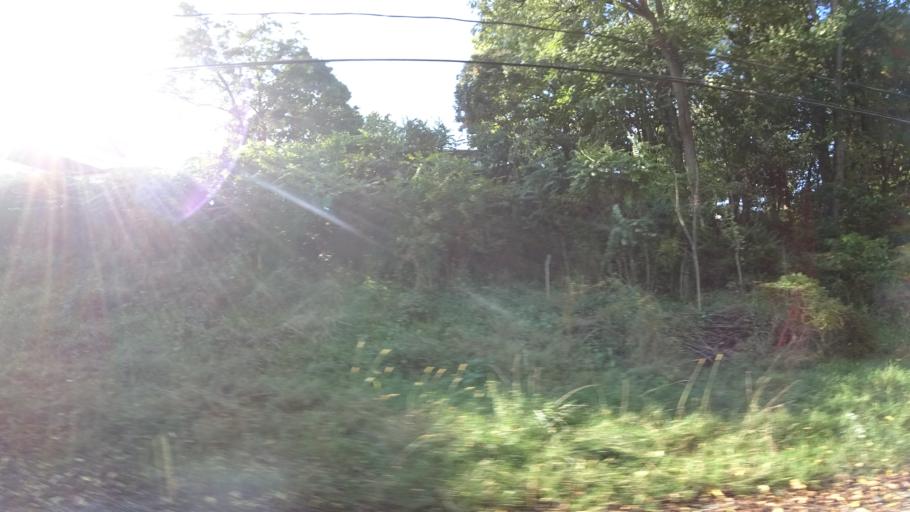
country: US
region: Michigan
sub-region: Saint Joseph County
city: Three Rivers
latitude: 41.9465
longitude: -85.6326
